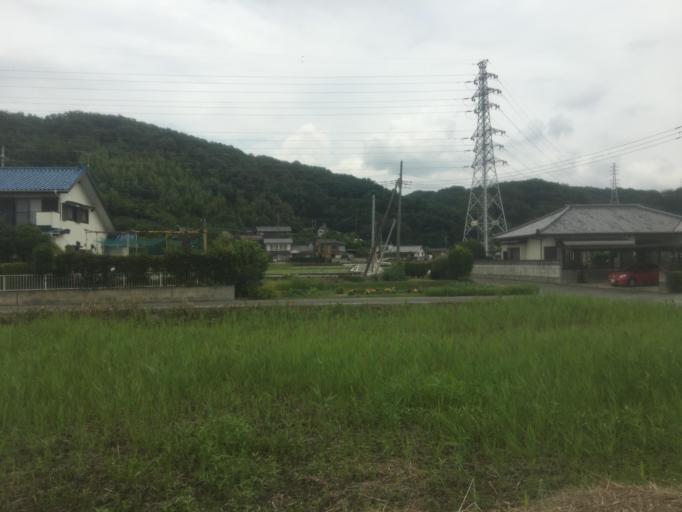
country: JP
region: Gunma
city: Fujioka
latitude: 36.2720
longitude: 139.0333
